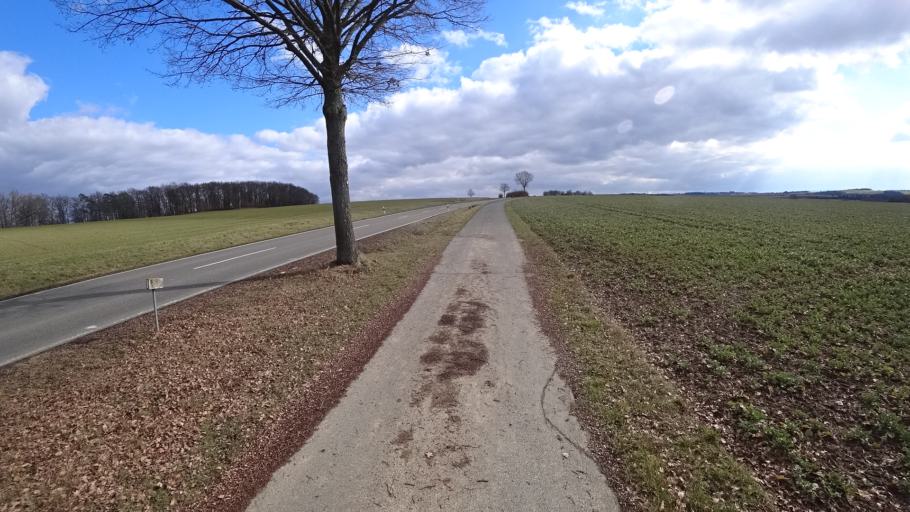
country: DE
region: Rheinland-Pfalz
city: Bornich
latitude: 50.1369
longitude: 7.7525
